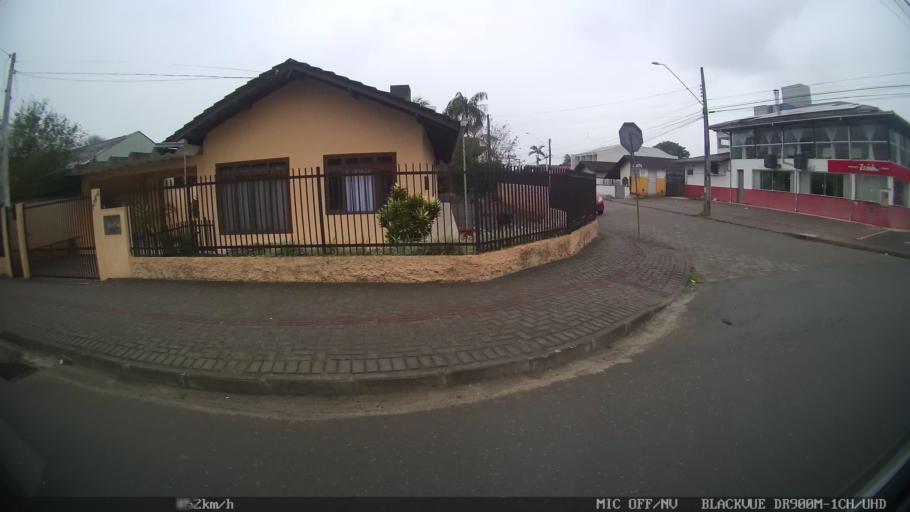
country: BR
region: Santa Catarina
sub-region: Joinville
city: Joinville
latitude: -26.2732
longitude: -48.8024
